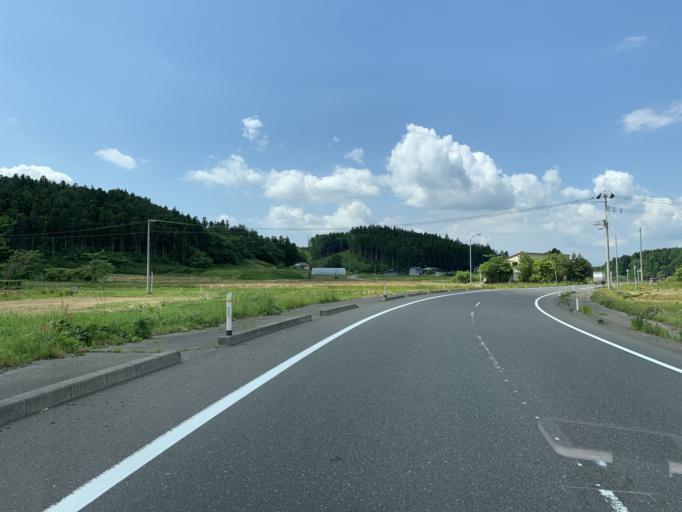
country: JP
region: Miyagi
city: Furukawa
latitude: 38.7305
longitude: 140.9574
